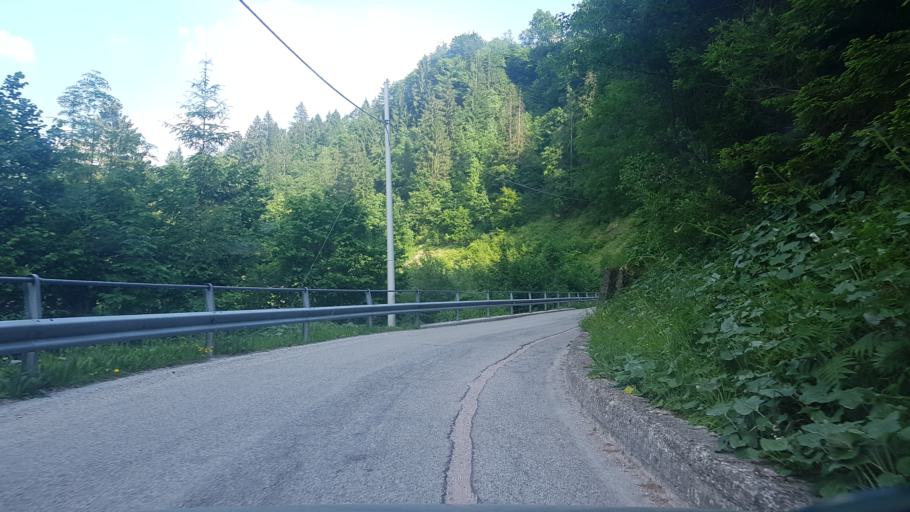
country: IT
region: Friuli Venezia Giulia
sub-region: Provincia di Udine
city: Pontebba
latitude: 46.5179
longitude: 13.2850
